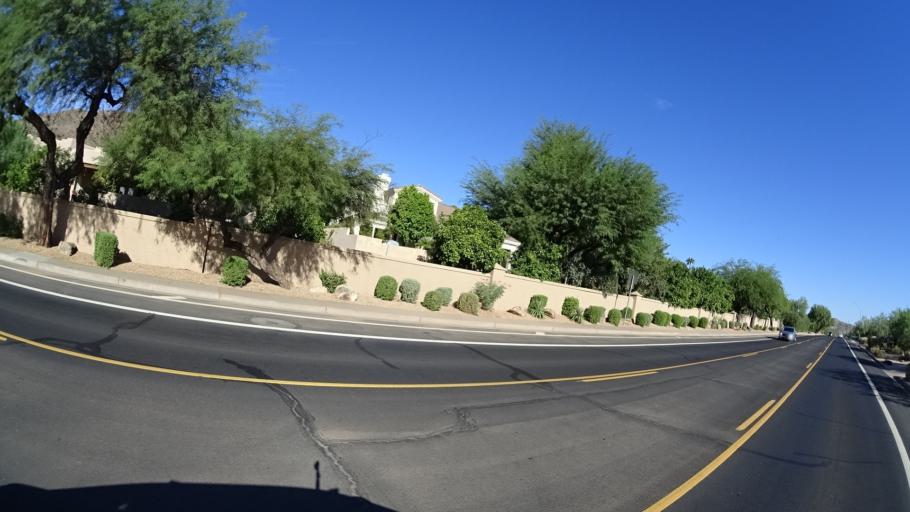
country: US
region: Arizona
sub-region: Maricopa County
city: Paradise Valley
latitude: 33.5138
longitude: -111.9432
